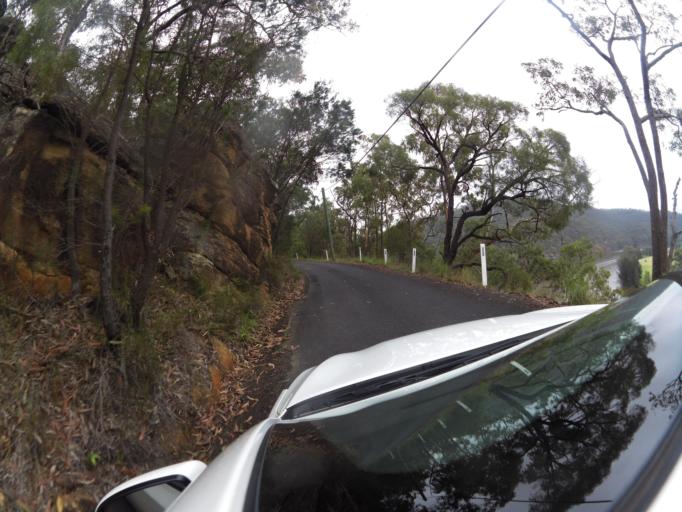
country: AU
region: New South Wales
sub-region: Hornsby Shire
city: Glenorie
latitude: -33.4274
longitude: 150.9531
